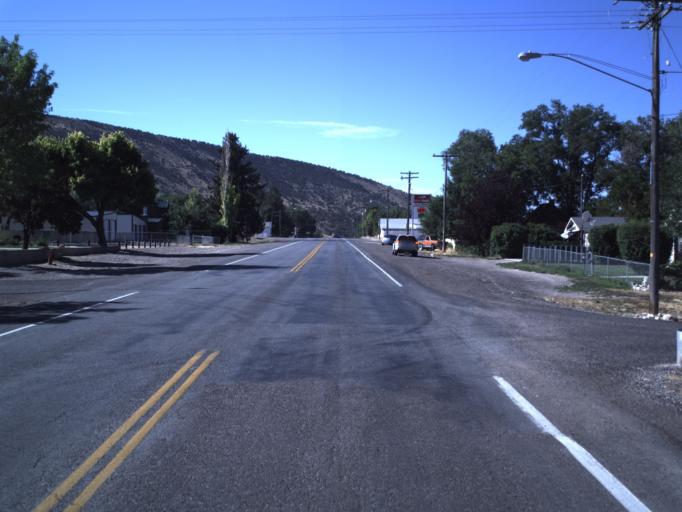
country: US
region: Utah
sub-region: Sanpete County
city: Manti
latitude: 39.1965
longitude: -111.6926
